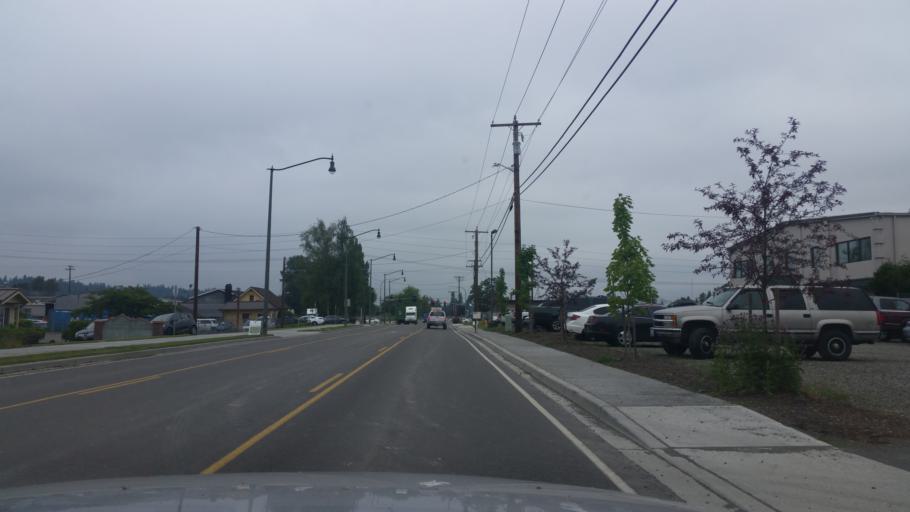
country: US
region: Washington
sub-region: King County
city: Pacific
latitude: 47.2483
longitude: -122.2488
